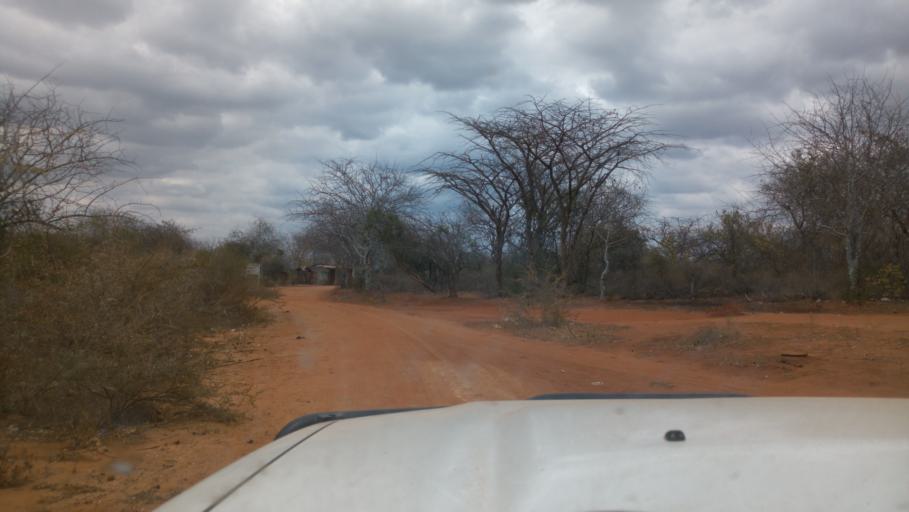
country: KE
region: Kitui
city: Kitui
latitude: -1.8850
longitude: 38.3787
